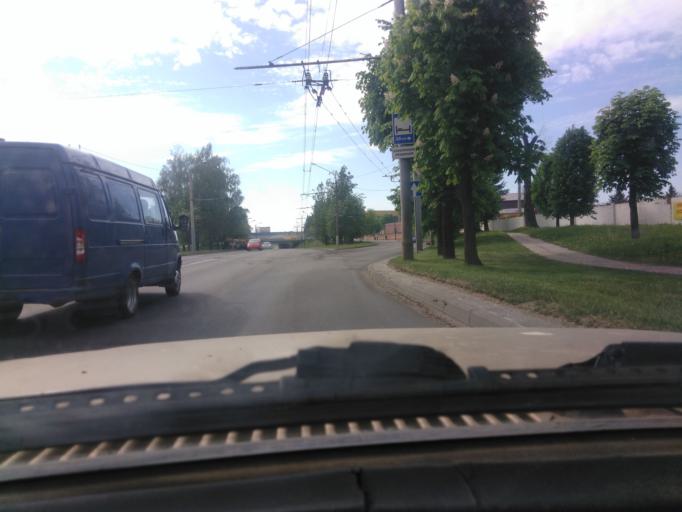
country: BY
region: Mogilev
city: Buynichy
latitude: 53.8944
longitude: 30.2975
